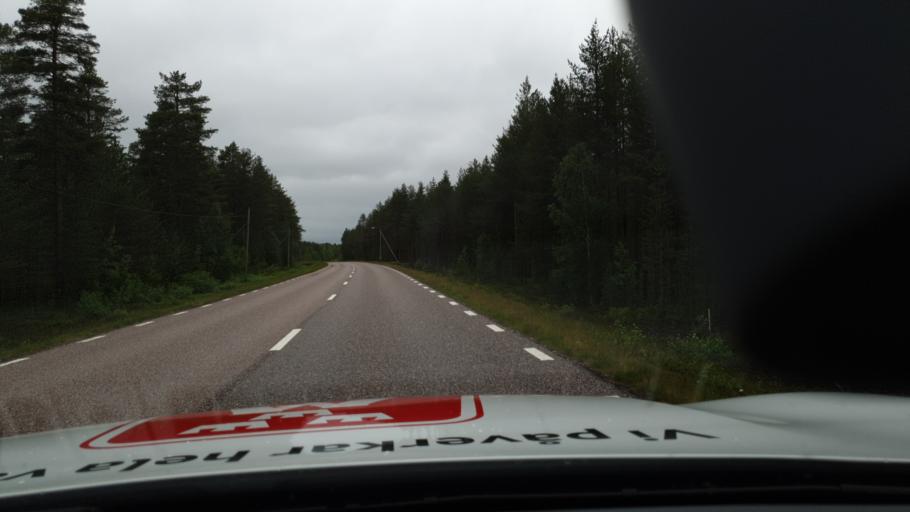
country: FI
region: Lapland
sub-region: Tunturi-Lappi
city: Kolari
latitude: 67.0216
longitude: 23.7268
